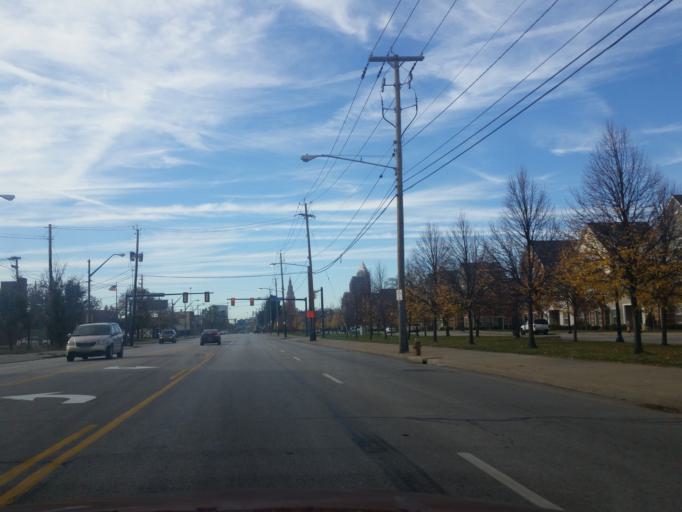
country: US
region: Ohio
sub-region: Cuyahoga County
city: Cleveland
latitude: 41.4901
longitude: -81.6615
